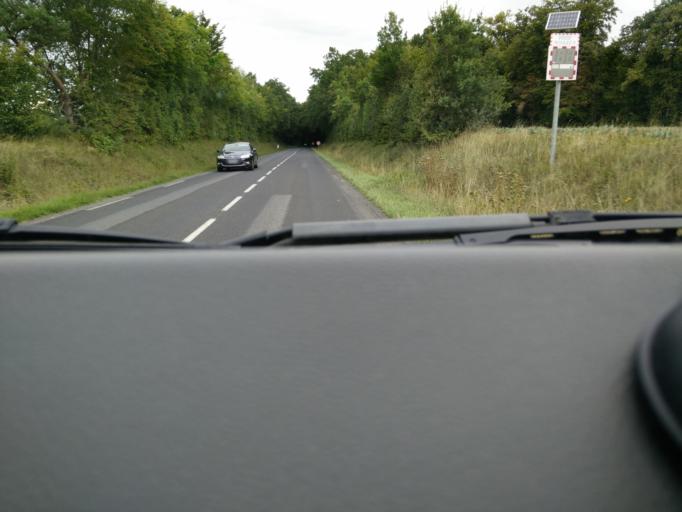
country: FR
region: Lorraine
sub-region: Departement de Meurthe-et-Moselle
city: Montauville
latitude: 48.9347
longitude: 5.8936
